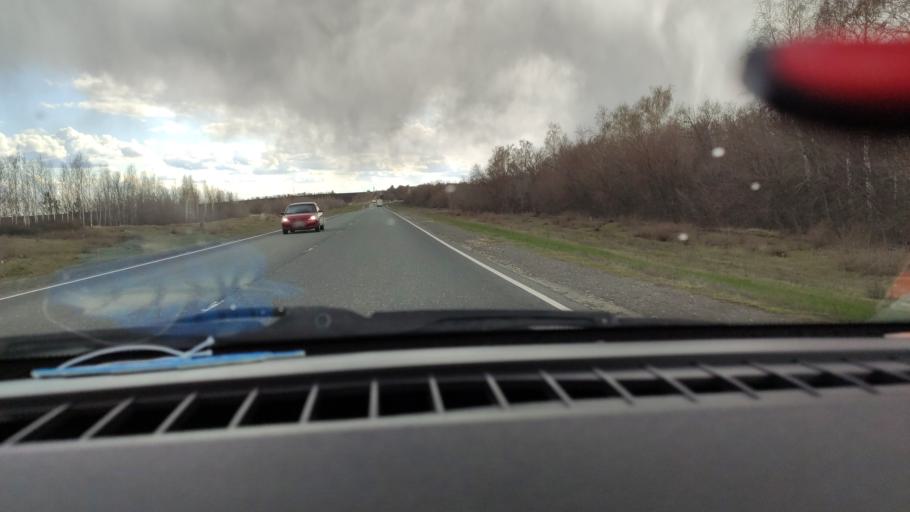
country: RU
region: Saratov
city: Balakovo
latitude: 52.1375
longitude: 47.7976
